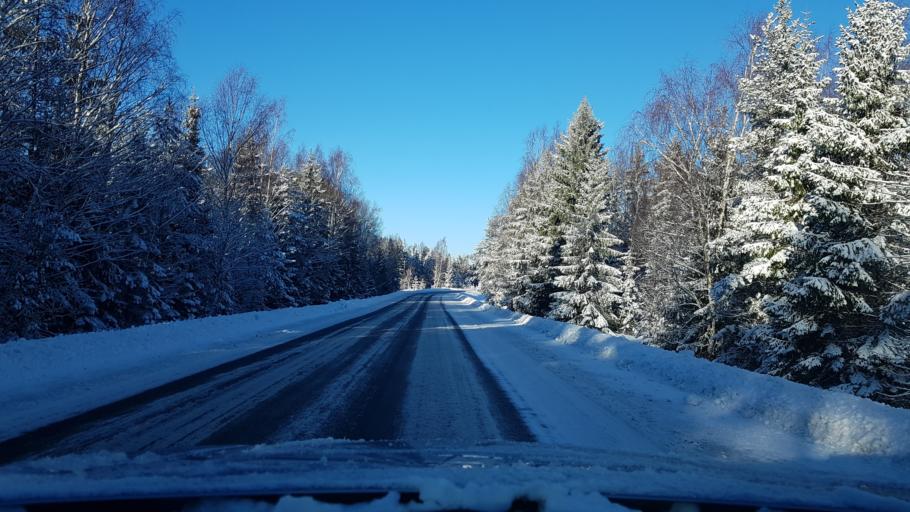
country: EE
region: Hiiumaa
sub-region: Kaerdla linn
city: Kardla
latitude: 58.9771
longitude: 22.8146
